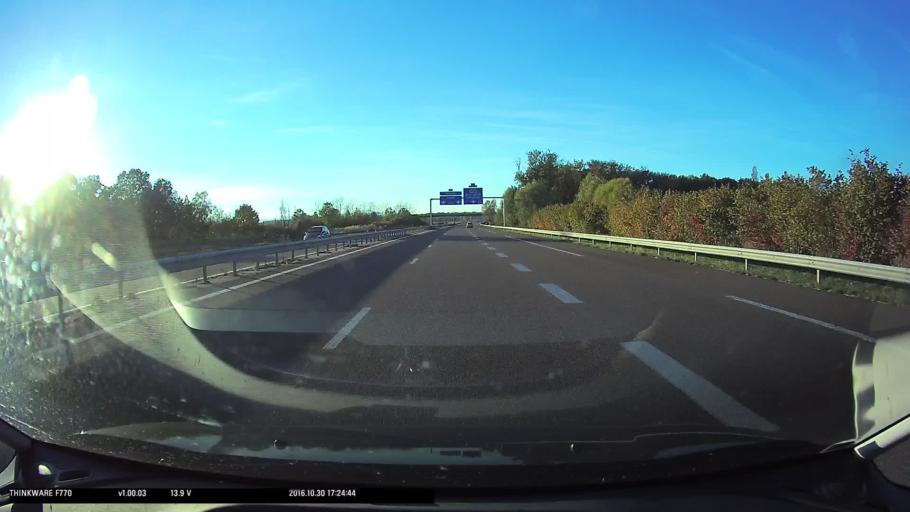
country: FR
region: Bourgogne
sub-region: Departement de la Cote-d'Or
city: Chevigny-Saint-Sauveur
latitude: 47.2702
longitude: 5.1617
